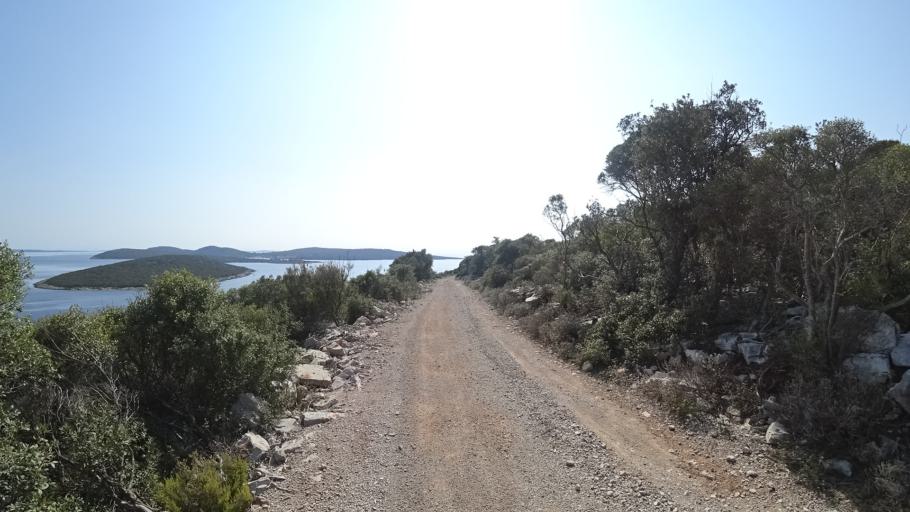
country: HR
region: Primorsko-Goranska
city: Mali Losinj
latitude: 44.4845
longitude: 14.5370
